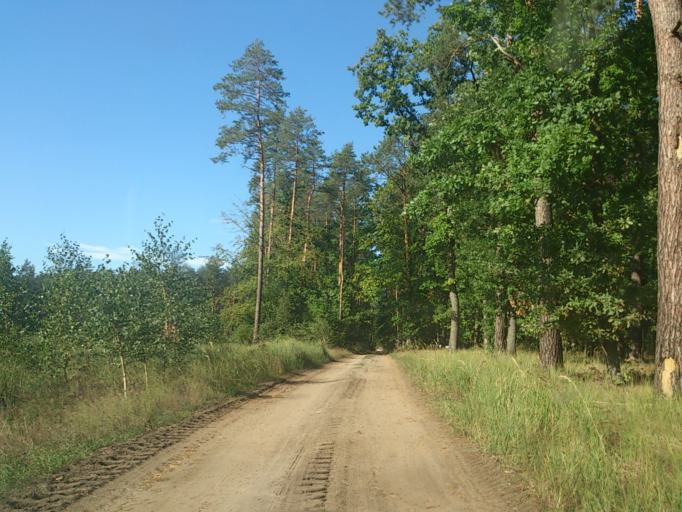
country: PL
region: Kujawsko-Pomorskie
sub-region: Powiat golubsko-dobrzynski
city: Radomin
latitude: 53.1379
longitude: 19.1464
